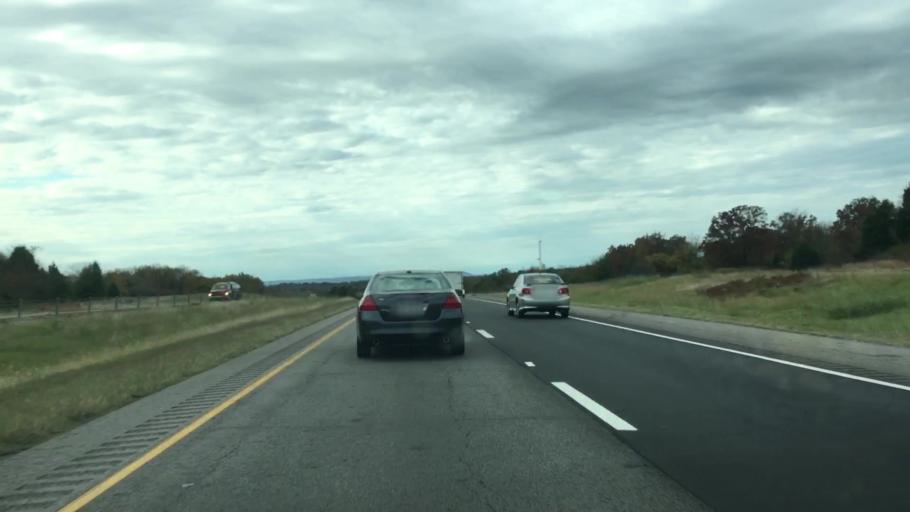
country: US
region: Arkansas
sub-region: Conway County
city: Morrilton
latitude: 35.1712
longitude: -92.6961
